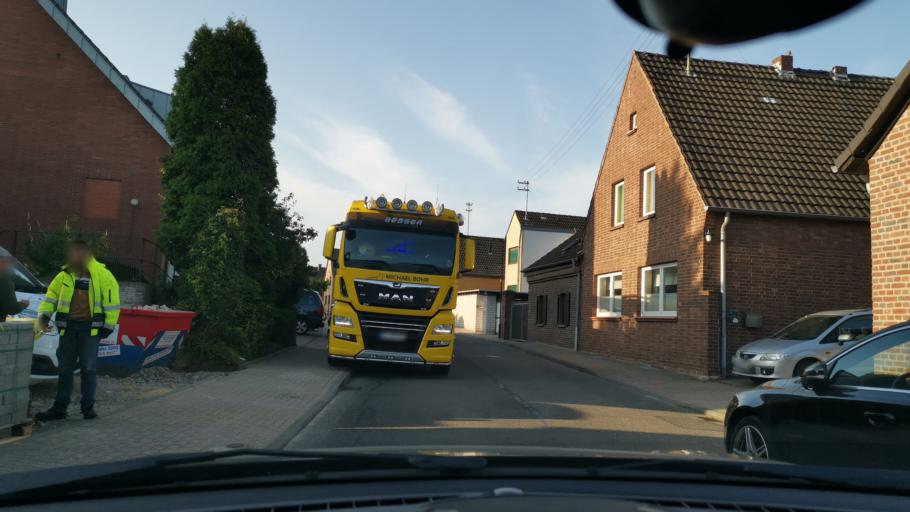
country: DE
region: North Rhine-Westphalia
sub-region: Regierungsbezirk Dusseldorf
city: Rommerskirchen
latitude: 51.0894
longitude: 6.6892
